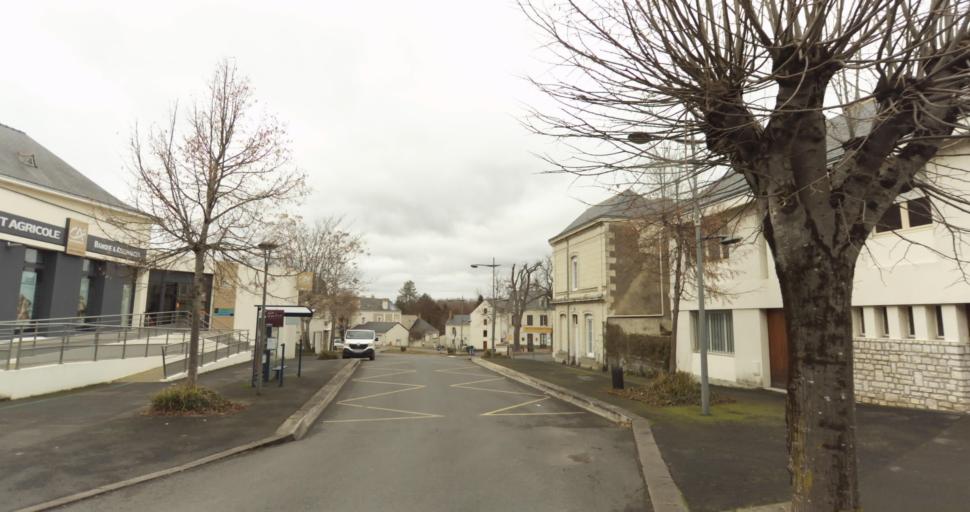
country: FR
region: Pays de la Loire
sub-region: Departement de Maine-et-Loire
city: Jumelles
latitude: 47.3802
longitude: -0.1080
